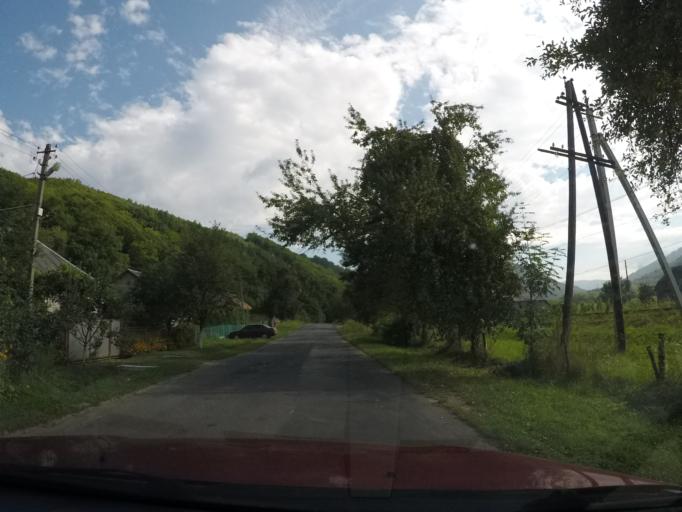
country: UA
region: Zakarpattia
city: Velykyi Bereznyi
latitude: 48.9325
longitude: 22.4609
